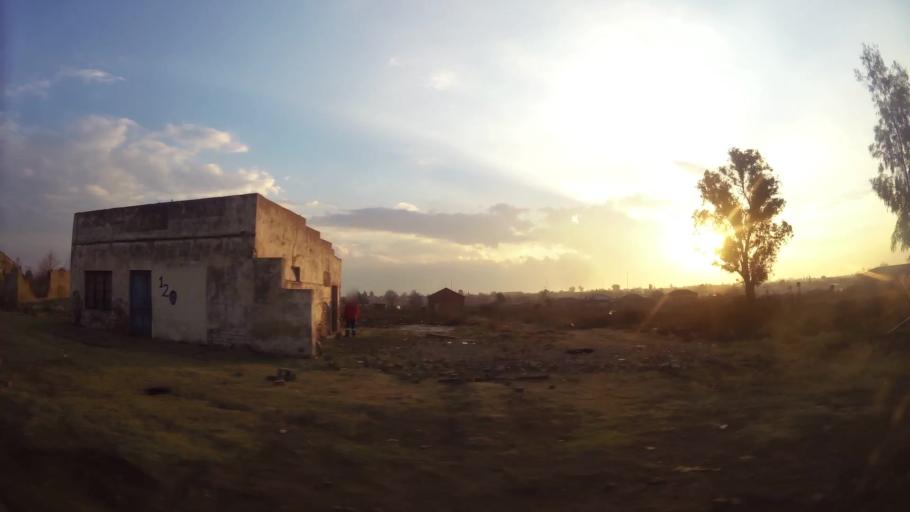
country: ZA
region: Gauteng
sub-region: City of Johannesburg Metropolitan Municipality
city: Orange Farm
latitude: -26.5378
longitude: 27.8857
